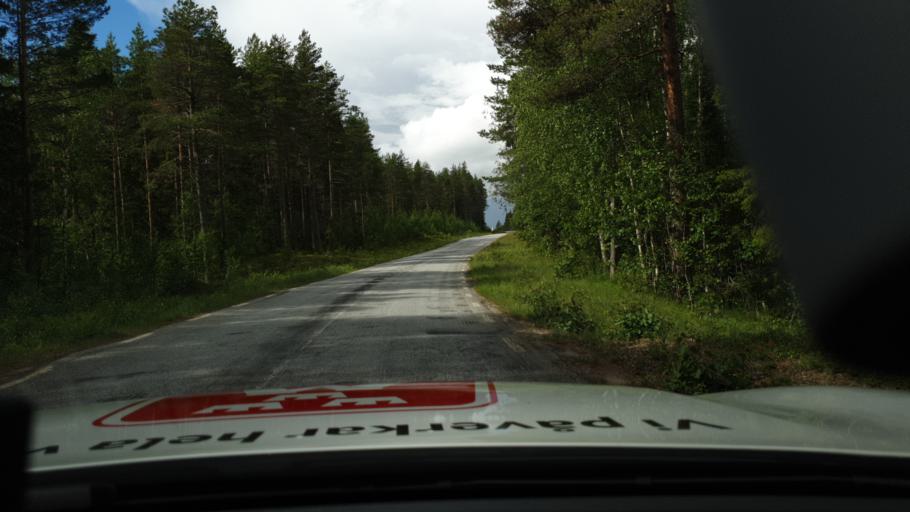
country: SE
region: Norrbotten
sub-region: Pitea Kommun
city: Rosvik
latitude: 65.4180
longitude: 21.7855
